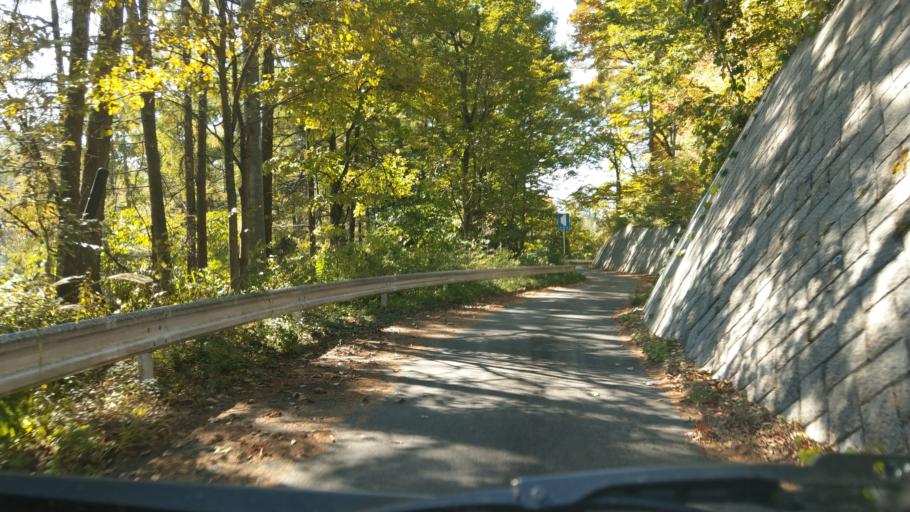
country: JP
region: Nagano
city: Komoro
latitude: 36.3766
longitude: 138.4252
